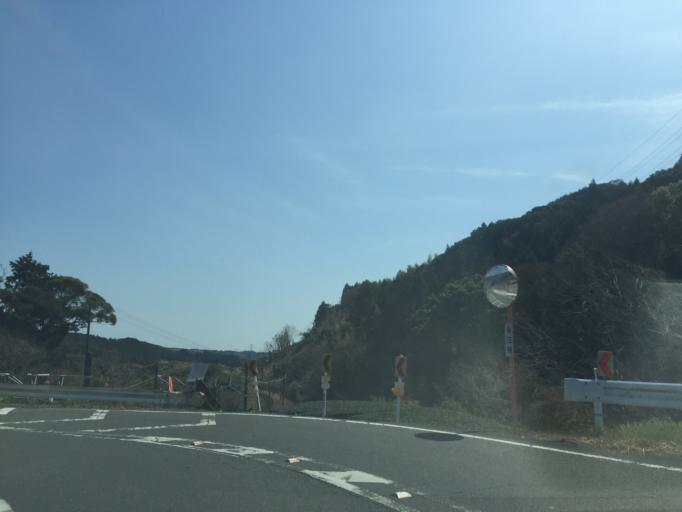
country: JP
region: Shizuoka
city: Kanaya
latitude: 34.8087
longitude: 138.1158
